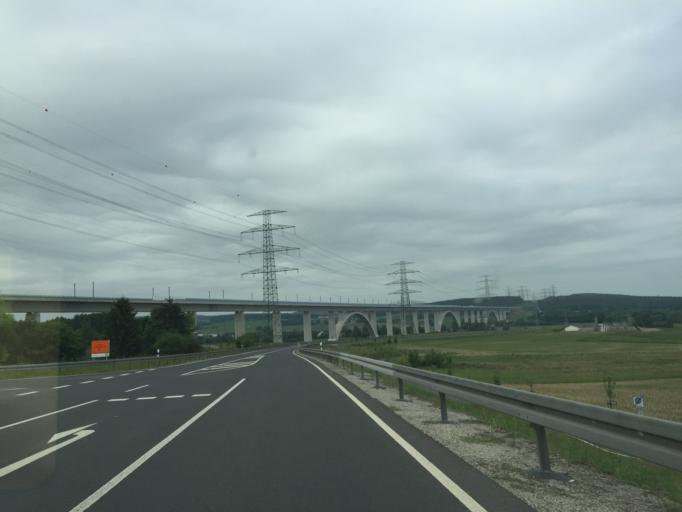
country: DE
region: Thuringia
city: Langewiesen
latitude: 50.6608
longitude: 10.9880
